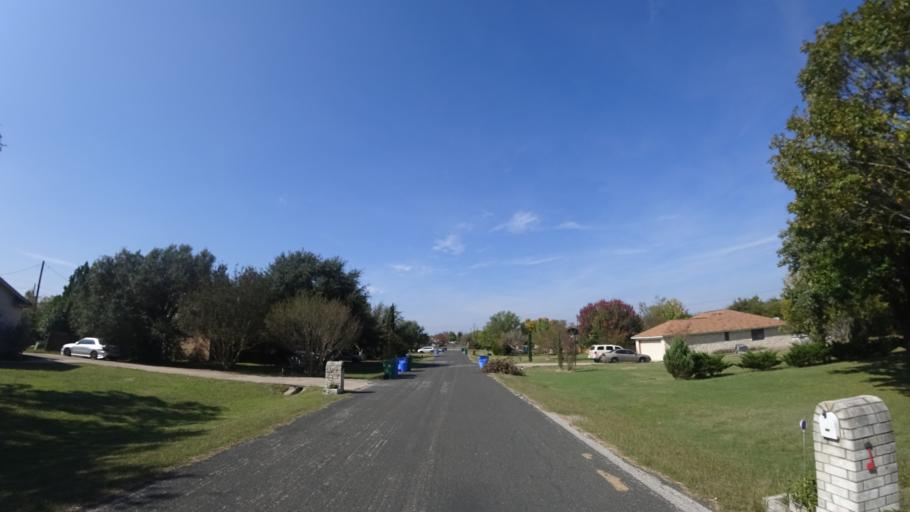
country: US
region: Texas
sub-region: Travis County
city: Pflugerville
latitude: 30.4218
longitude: -97.6262
